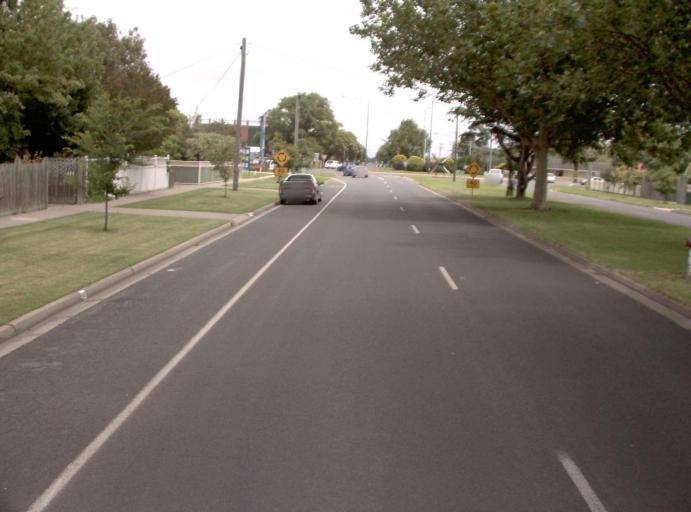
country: AU
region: Victoria
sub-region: Wellington
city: Sale
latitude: -38.0986
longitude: 147.0695
